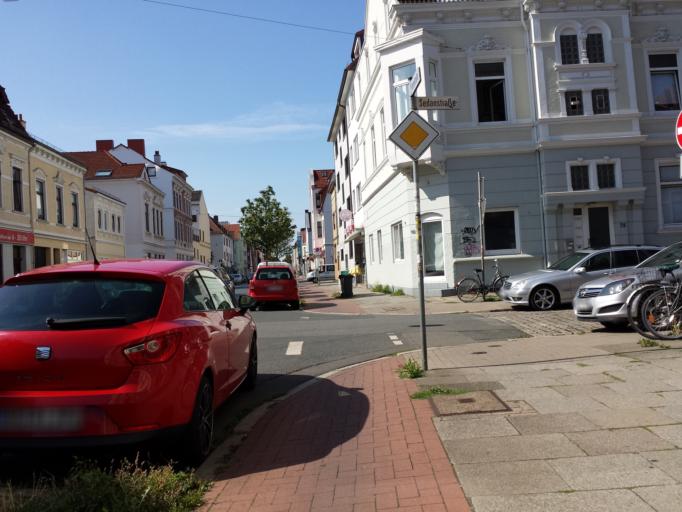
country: DE
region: Bremen
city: Bremen
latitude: 53.0652
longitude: 8.8002
